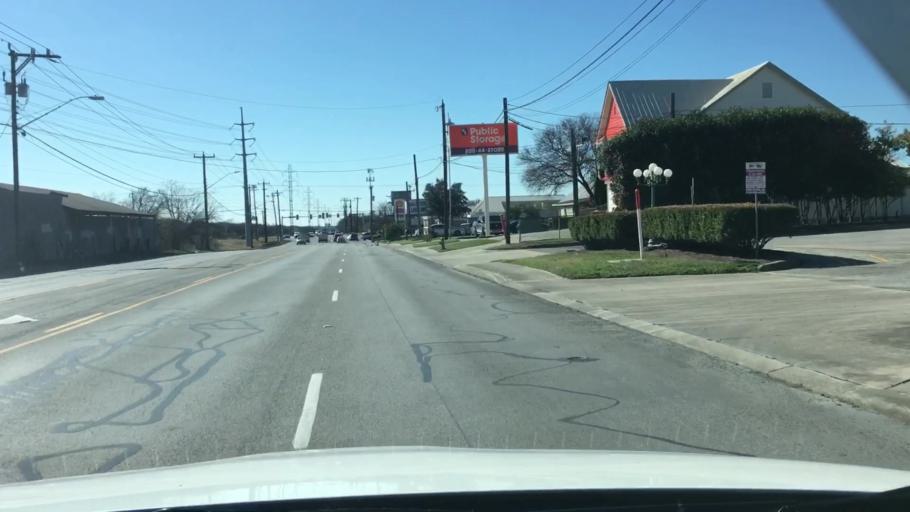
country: US
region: Texas
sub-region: Bexar County
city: Windcrest
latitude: 29.5634
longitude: -98.4203
